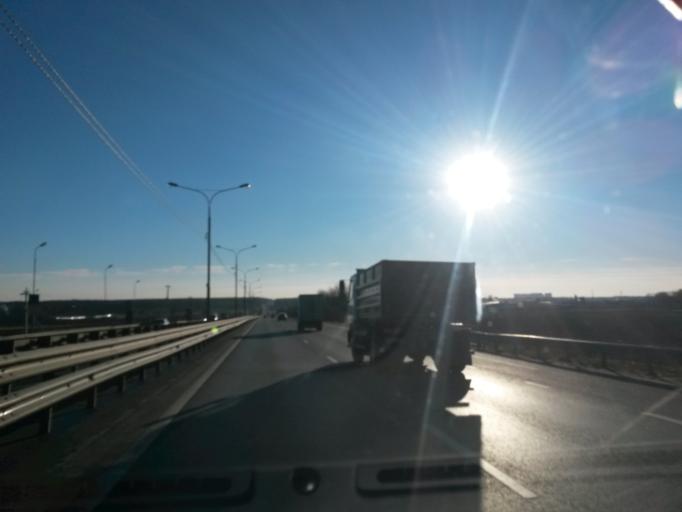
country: RU
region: Moskovskaya
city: Lesnoy
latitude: 56.0578
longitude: 37.8992
